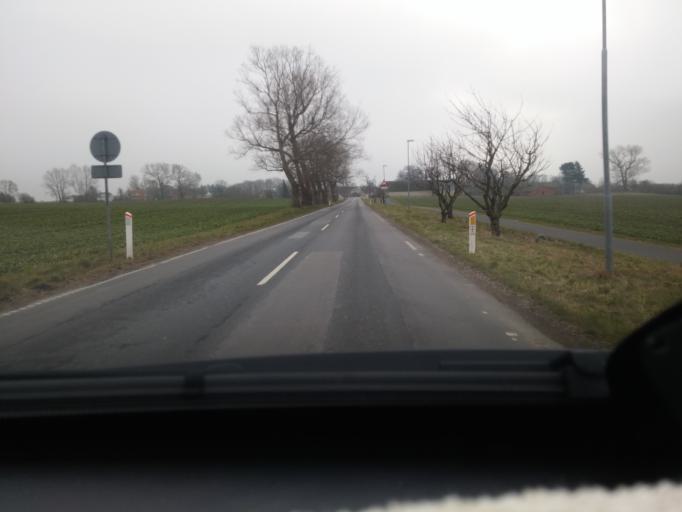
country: DK
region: South Denmark
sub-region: Nyborg Kommune
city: Ullerslev
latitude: 55.3605
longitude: 10.7278
